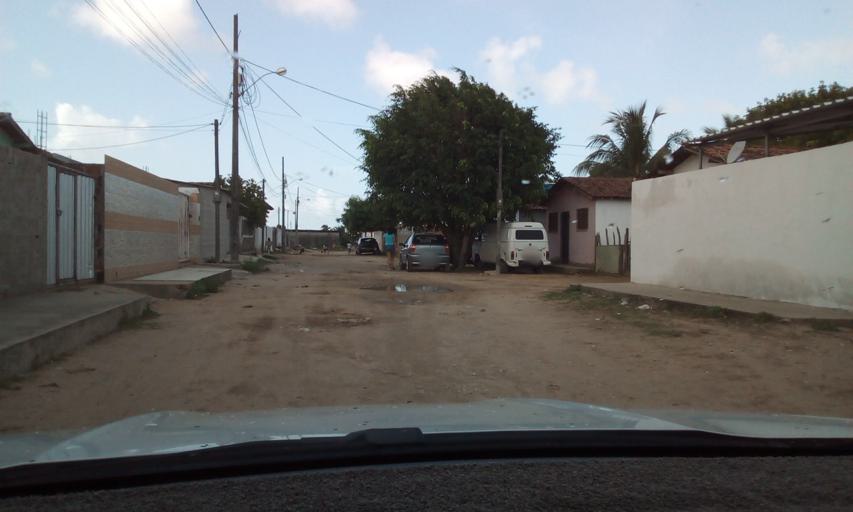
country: BR
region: Paraiba
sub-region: Joao Pessoa
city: Joao Pessoa
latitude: -7.1696
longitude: -34.8235
